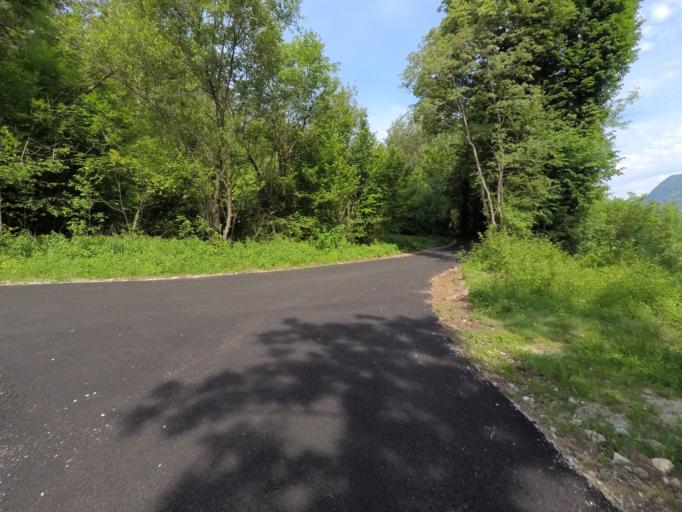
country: IT
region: Friuli Venezia Giulia
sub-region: Provincia di Udine
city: Cavazzo Carnico
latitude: 46.3599
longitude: 13.0551
